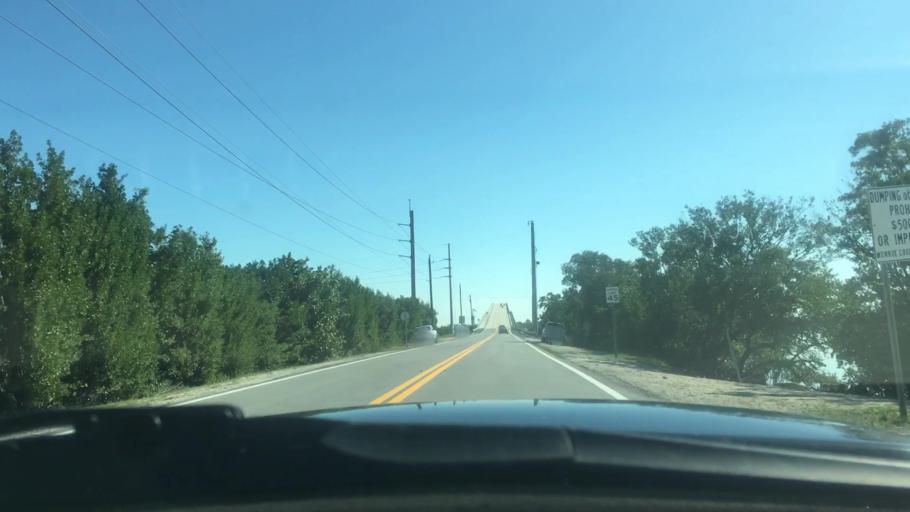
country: US
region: Florida
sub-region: Monroe County
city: North Key Largo
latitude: 25.2899
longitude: -80.3747
